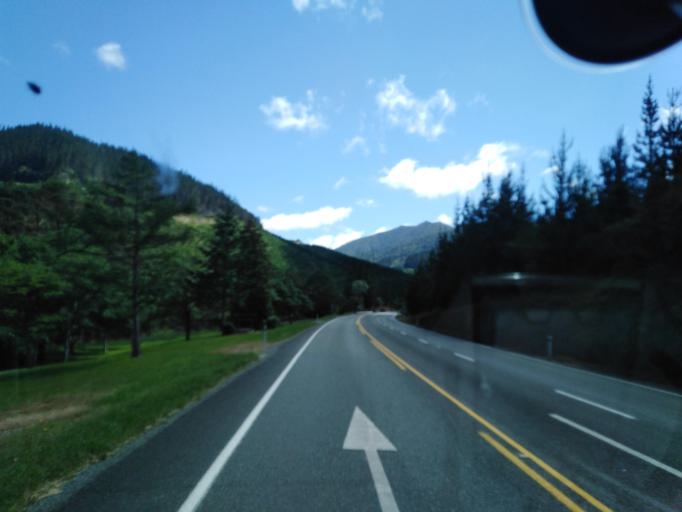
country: NZ
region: Nelson
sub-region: Nelson City
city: Nelson
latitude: -41.1802
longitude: 173.5601
